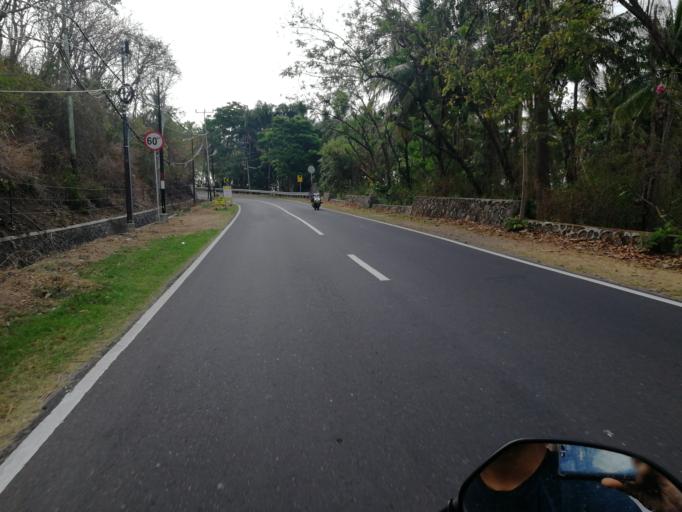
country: ID
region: West Nusa Tenggara
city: Karangsubagan
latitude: -8.4438
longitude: 116.0383
